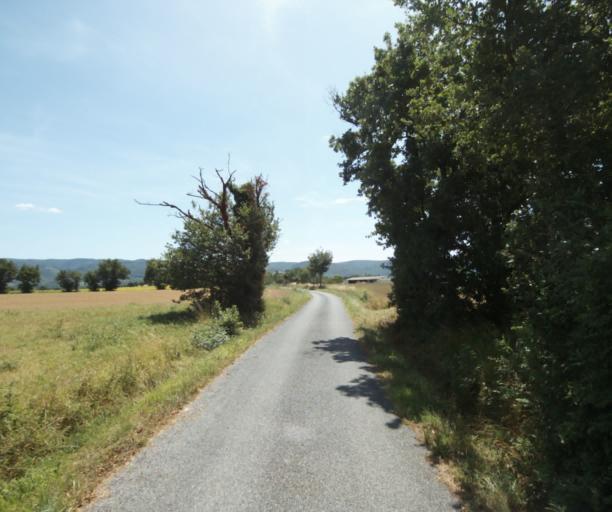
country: FR
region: Midi-Pyrenees
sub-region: Departement du Tarn
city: Soreze
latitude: 43.4887
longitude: 2.0612
